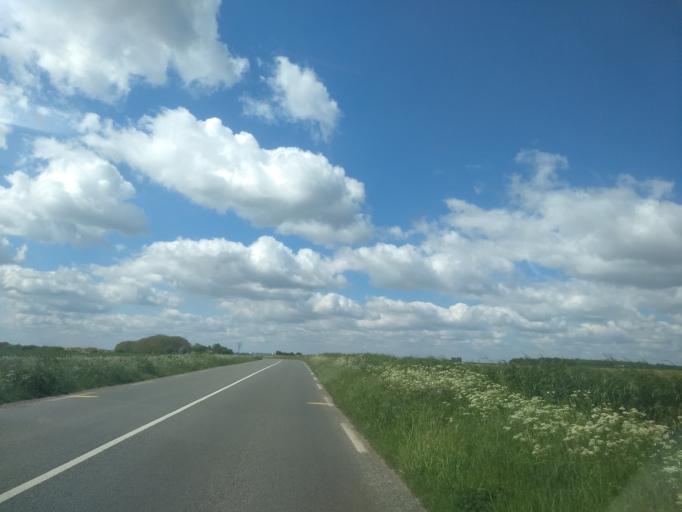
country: FR
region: Nord-Pas-de-Calais
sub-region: Departement du Pas-de-Calais
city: Bailleul-Sir-Berthoult
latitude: 50.3328
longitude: 2.8347
